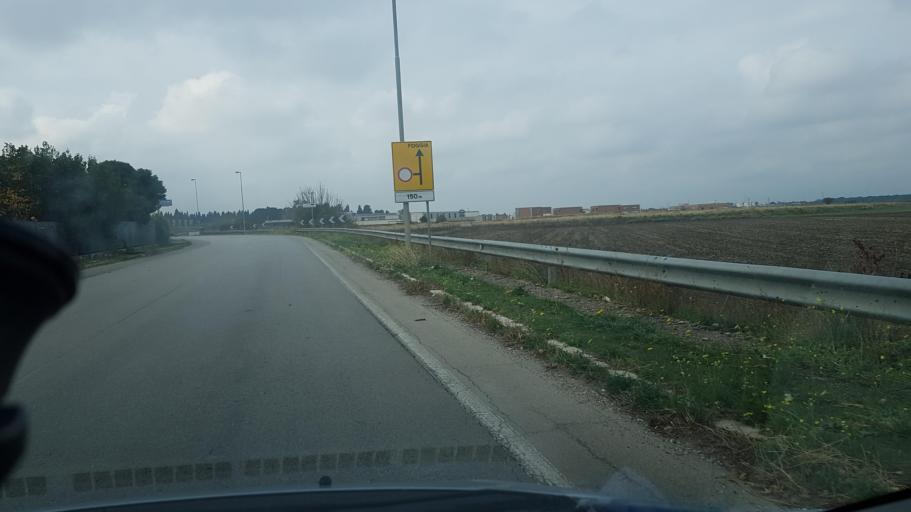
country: IT
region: Apulia
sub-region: Provincia di Foggia
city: Foggia
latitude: 41.4796
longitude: 15.5560
